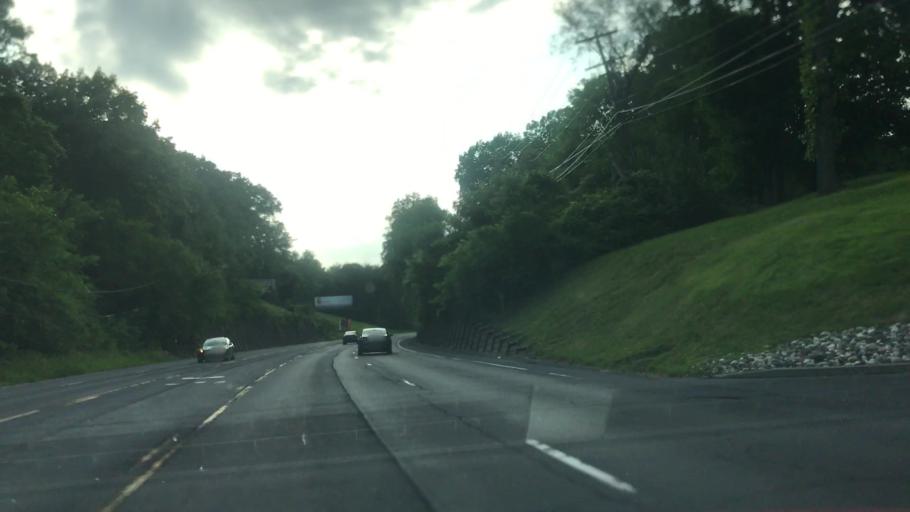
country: US
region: New York
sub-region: Albany County
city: Watervliet
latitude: 42.7343
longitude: -73.7170
